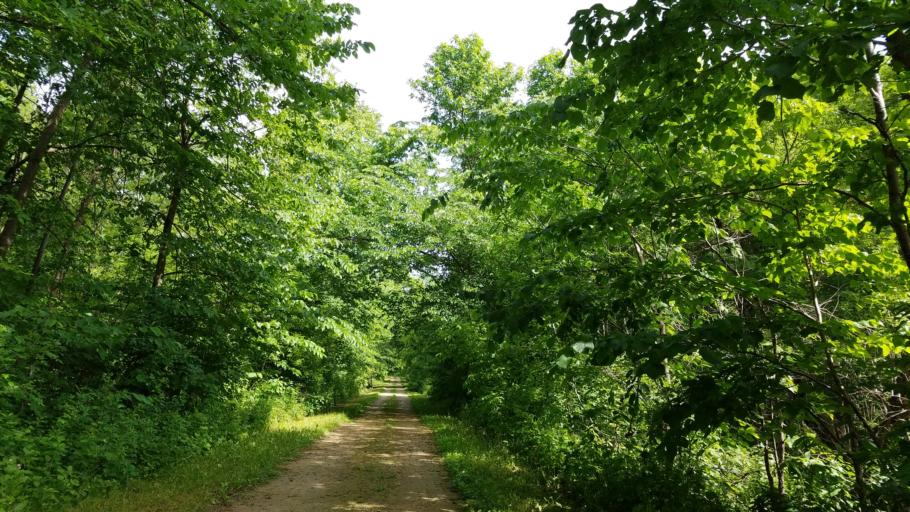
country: US
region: Wisconsin
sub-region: Dunn County
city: Menomonie
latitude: 44.7809
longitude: -91.9416
